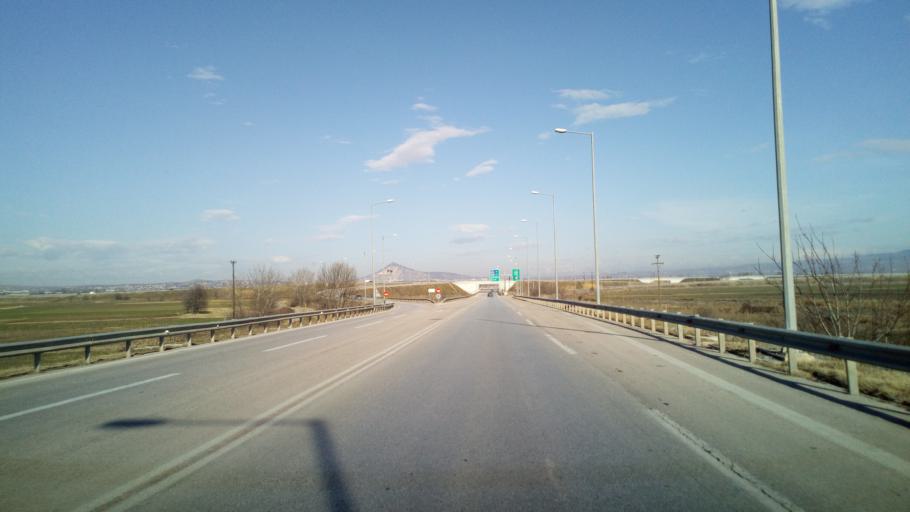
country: GR
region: Central Macedonia
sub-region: Nomos Thessalonikis
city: Lagyna
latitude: 40.7334
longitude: 23.0128
